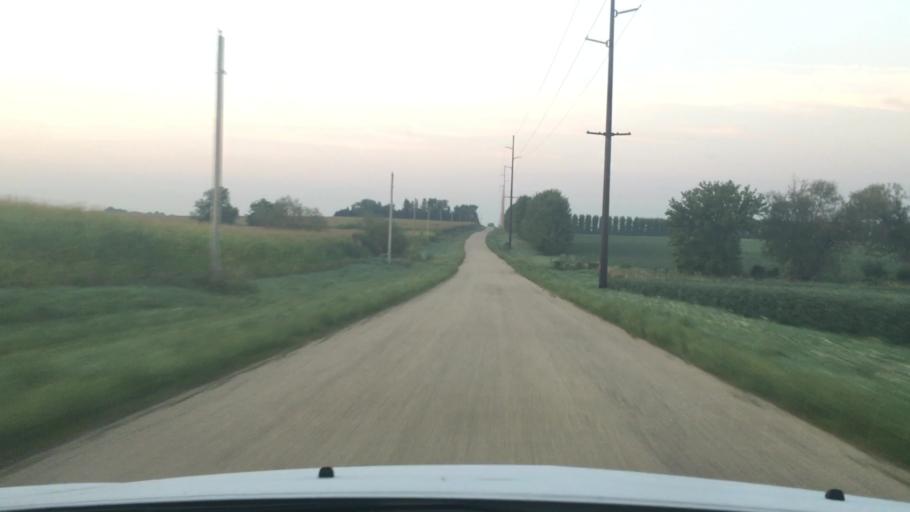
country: US
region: Illinois
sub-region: Ogle County
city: Rochelle
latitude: 41.8791
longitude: -89.0010
